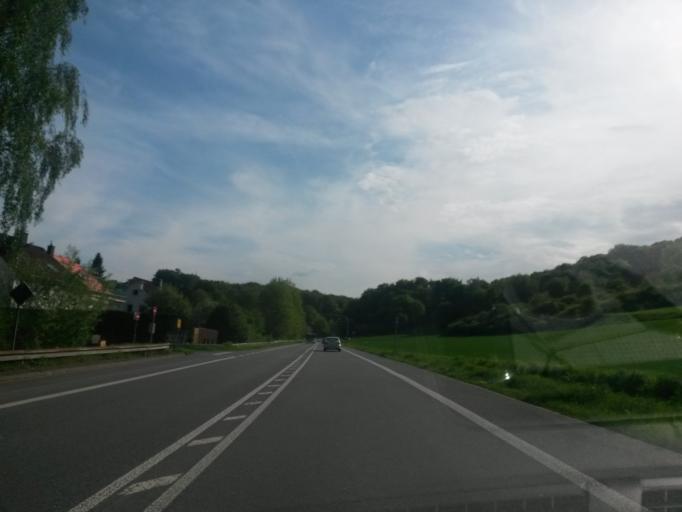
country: DE
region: North Rhine-Westphalia
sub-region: Regierungsbezirk Arnsberg
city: Hagen
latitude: 51.3558
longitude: 7.5467
